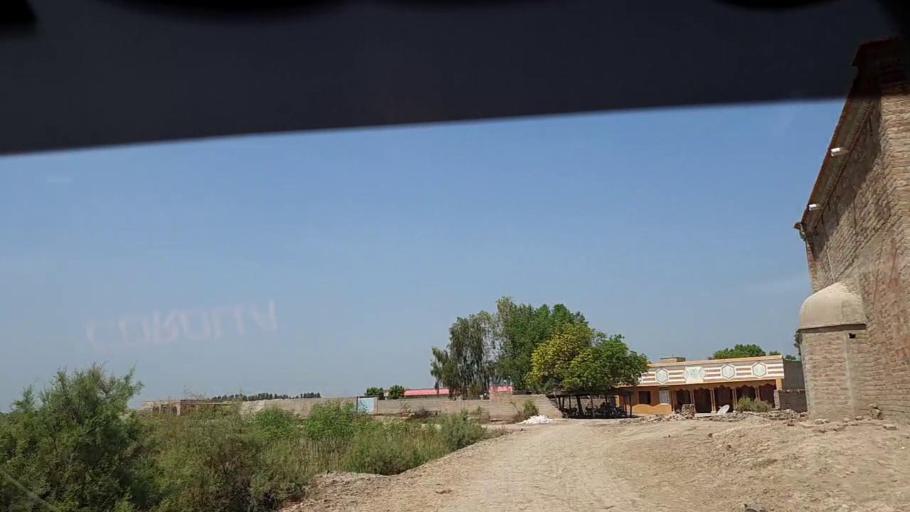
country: PK
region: Sindh
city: Ghauspur
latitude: 28.1756
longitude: 69.0671
